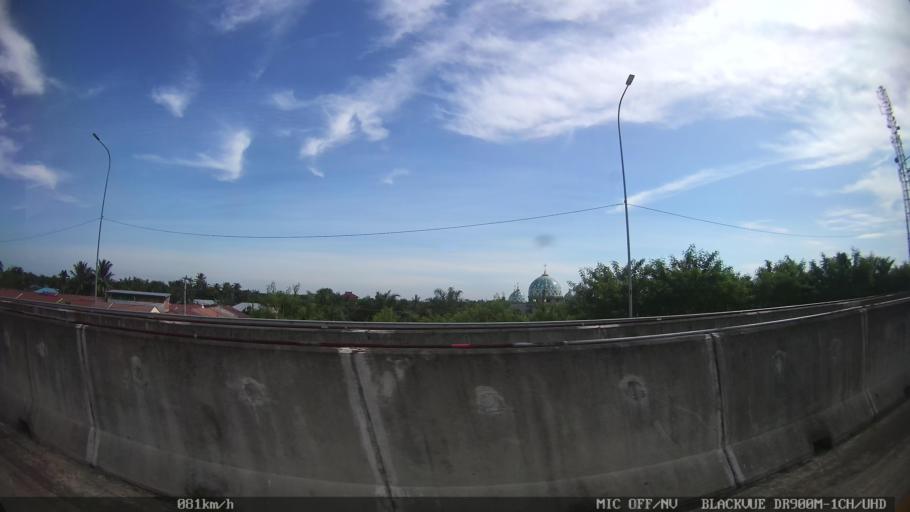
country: ID
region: North Sumatra
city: Binjai
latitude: 3.6458
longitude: 98.5521
